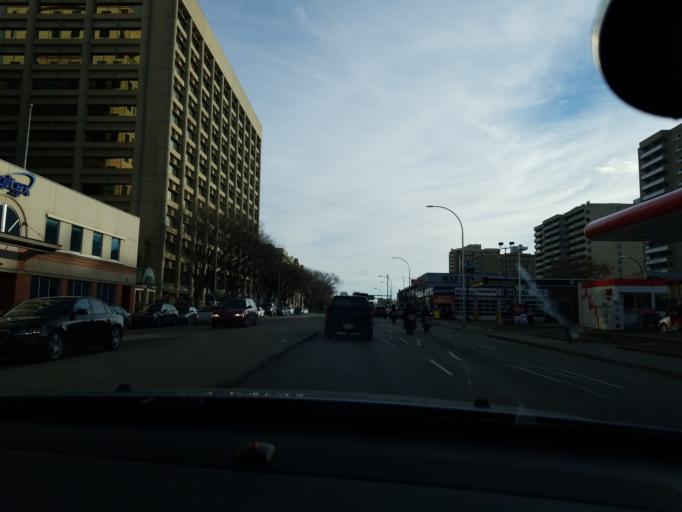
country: CA
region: Alberta
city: Edmonton
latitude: 53.5386
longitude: -113.5086
